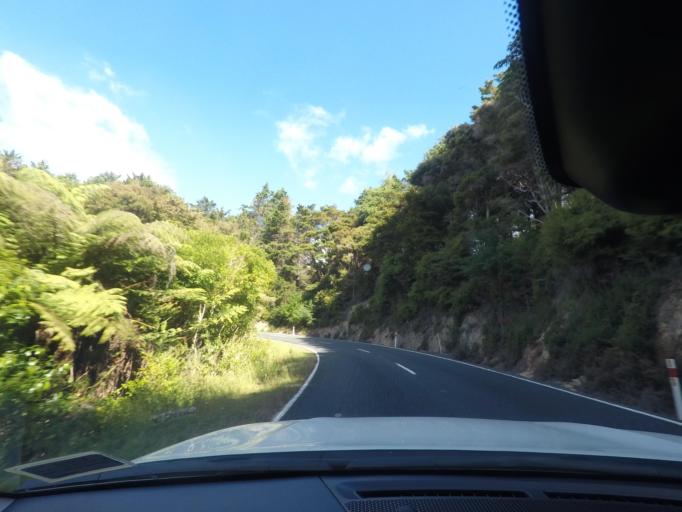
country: NZ
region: Northland
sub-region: Whangarei
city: Ngunguru
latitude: -35.6725
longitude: 174.4660
